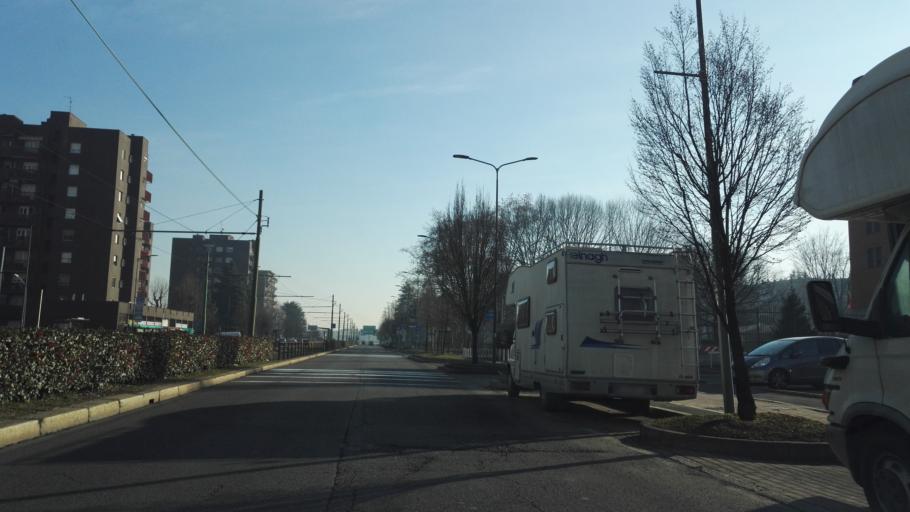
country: IT
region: Lombardy
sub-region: Citta metropolitana di Milano
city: Linate
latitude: 45.4499
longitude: 9.2521
